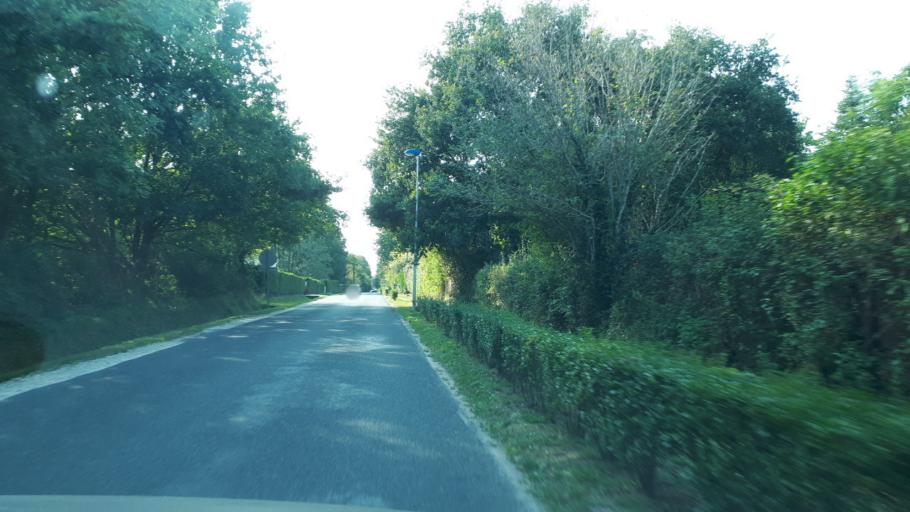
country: FR
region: Centre
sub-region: Departement du Cher
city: Saint-Eloy-de-Gy
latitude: 47.2250
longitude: 2.3146
